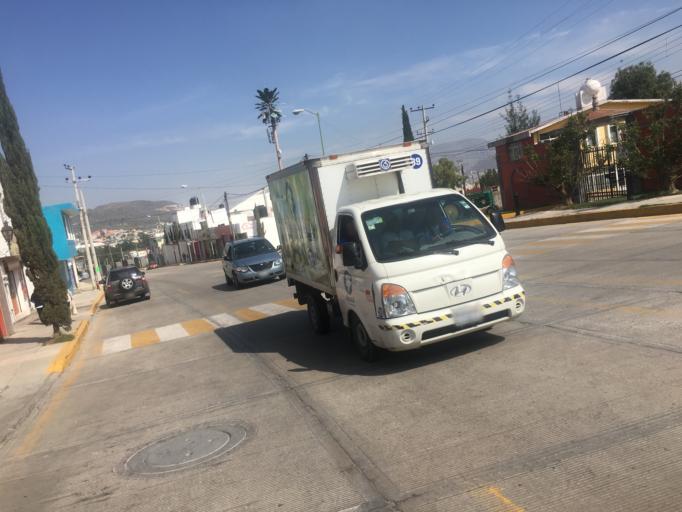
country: MX
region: Hidalgo
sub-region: Mineral de la Reforma
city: Carboneras
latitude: 20.0912
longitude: -98.7061
